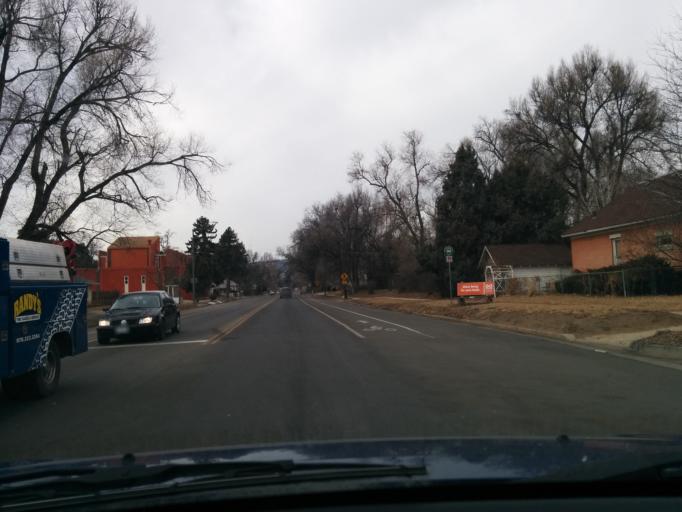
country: US
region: Colorado
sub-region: Larimer County
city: Fort Collins
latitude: 40.5922
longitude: -105.0843
